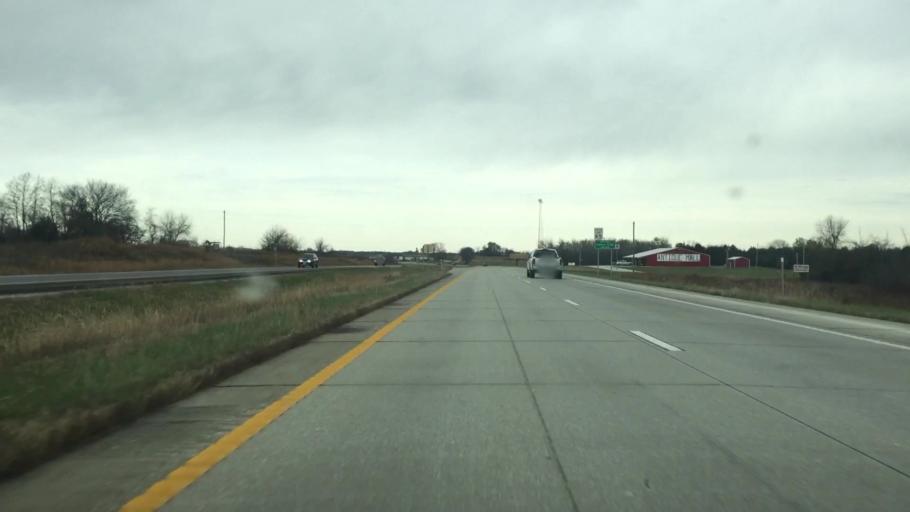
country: US
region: Missouri
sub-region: Saint Clair County
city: Osceola
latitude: 38.1207
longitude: -93.7058
